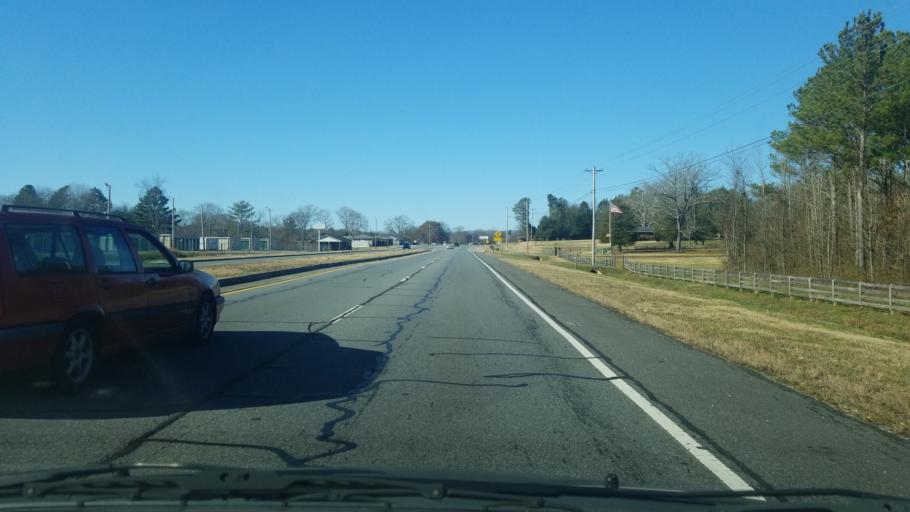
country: US
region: Georgia
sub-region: Catoosa County
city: Indian Springs
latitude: 34.9575
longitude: -85.2099
